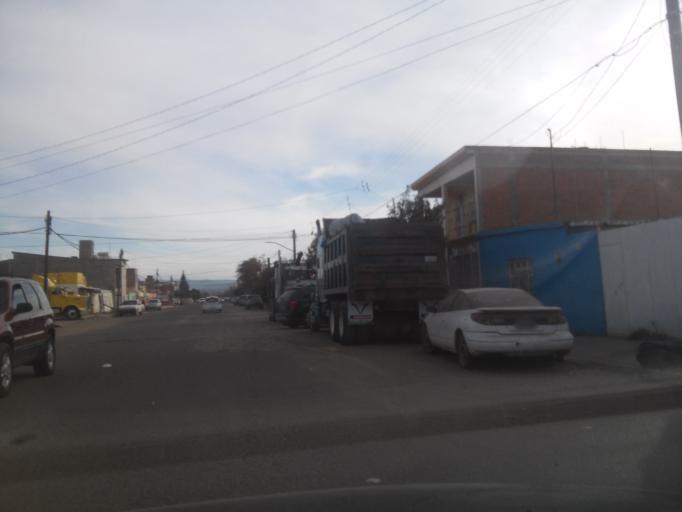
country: MX
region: Durango
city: Victoria de Durango
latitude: 24.0234
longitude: -104.6351
